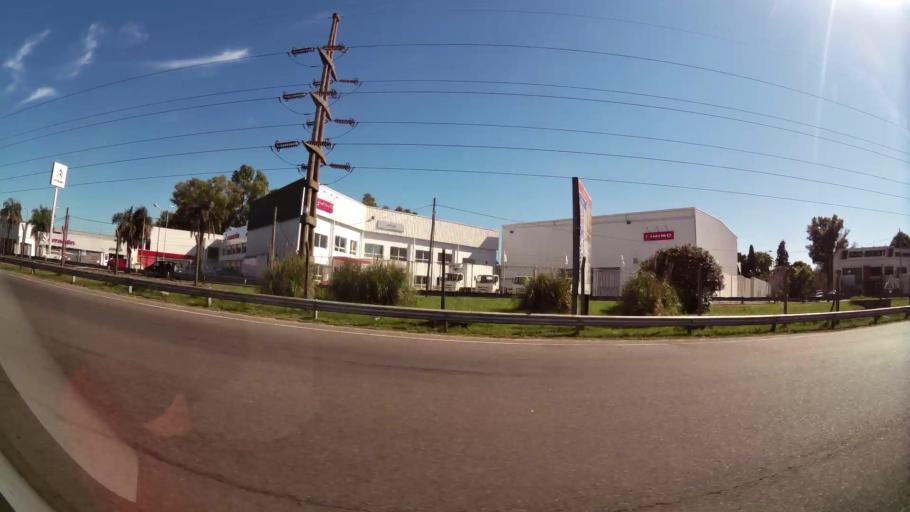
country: AR
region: Buenos Aires
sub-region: Partido de Tigre
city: Tigre
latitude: -34.4835
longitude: -58.6256
